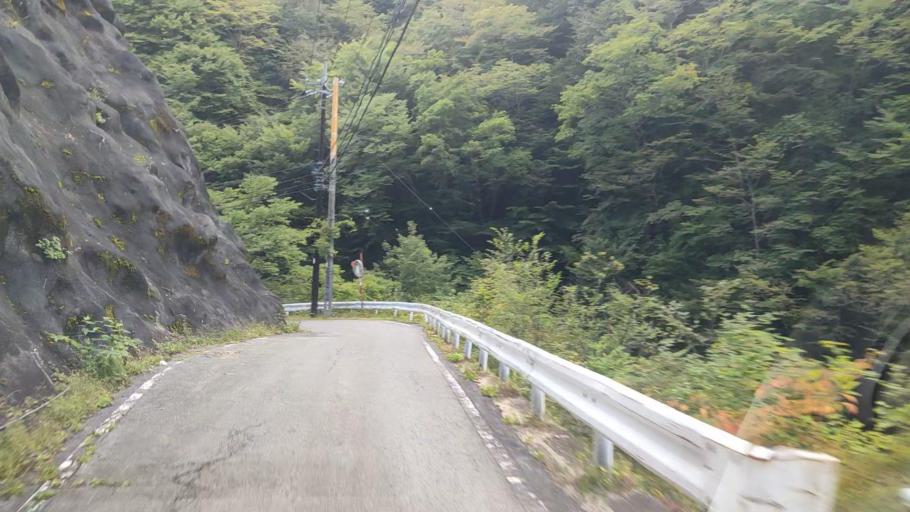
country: JP
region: Gunma
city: Nakanojomachi
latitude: 36.6489
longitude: 138.6407
